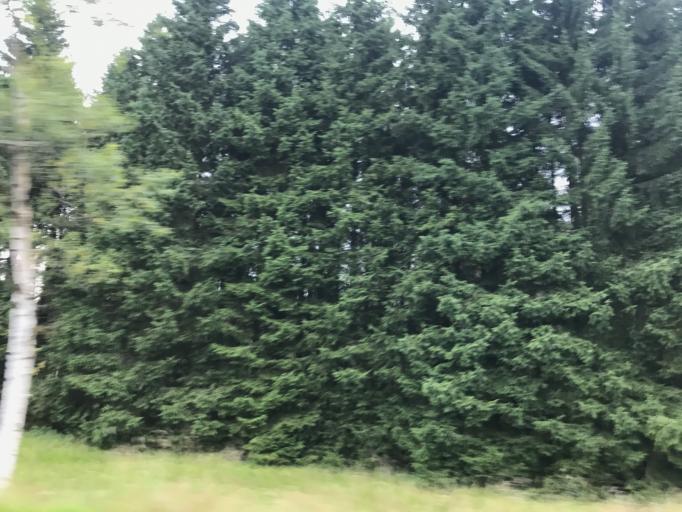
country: DE
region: Lower Saxony
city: Sankt Andreasberg
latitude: 51.7755
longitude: 10.5520
